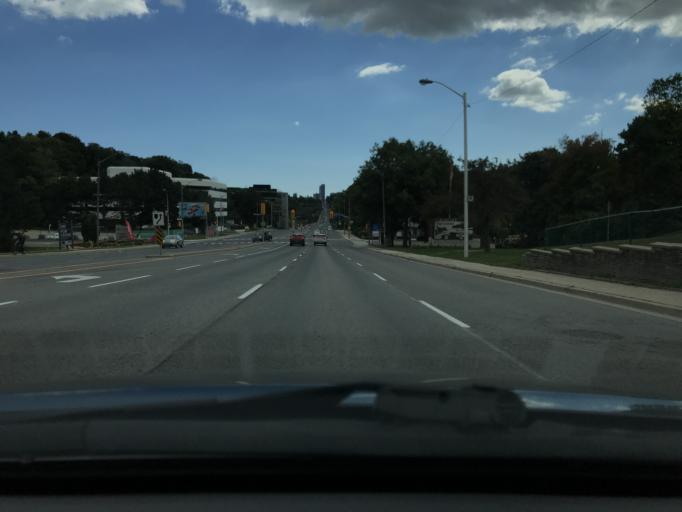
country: CA
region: Ontario
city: Willowdale
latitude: 43.7483
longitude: -79.4077
